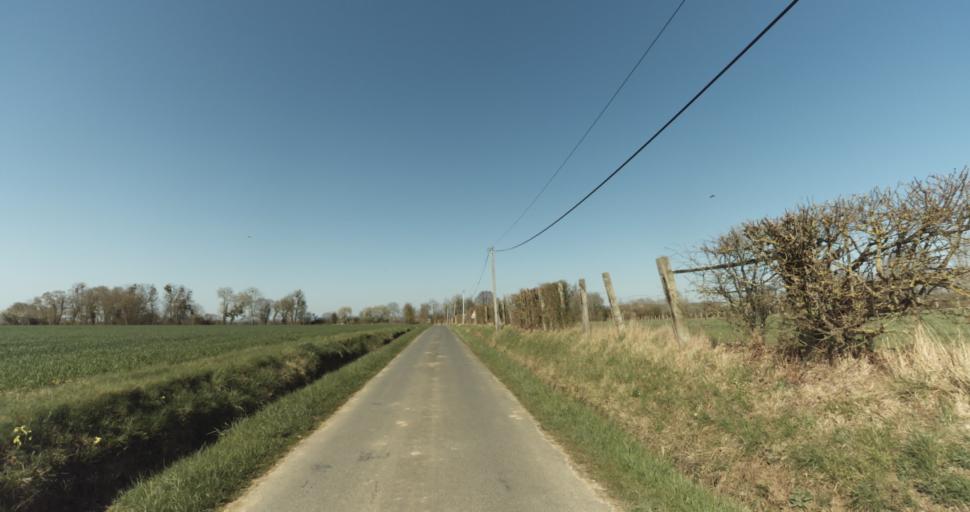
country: FR
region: Lower Normandy
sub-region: Departement du Calvados
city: Saint-Pierre-sur-Dives
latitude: 48.9396
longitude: -0.0075
